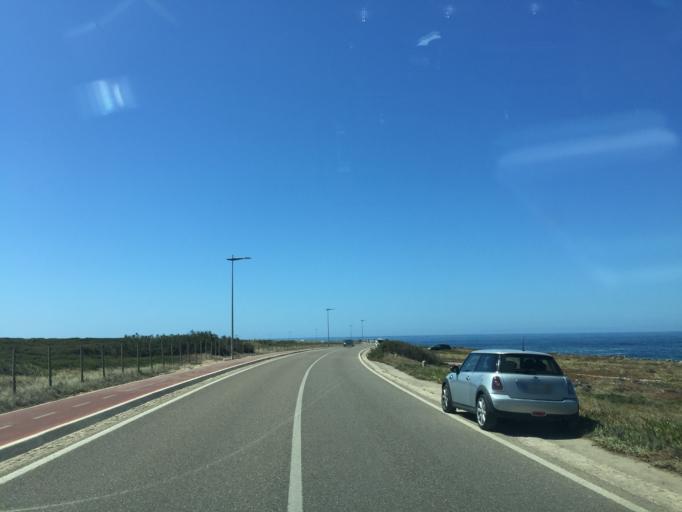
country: PT
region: Lisbon
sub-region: Cascais
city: Cascais
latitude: 38.7171
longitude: -9.4806
